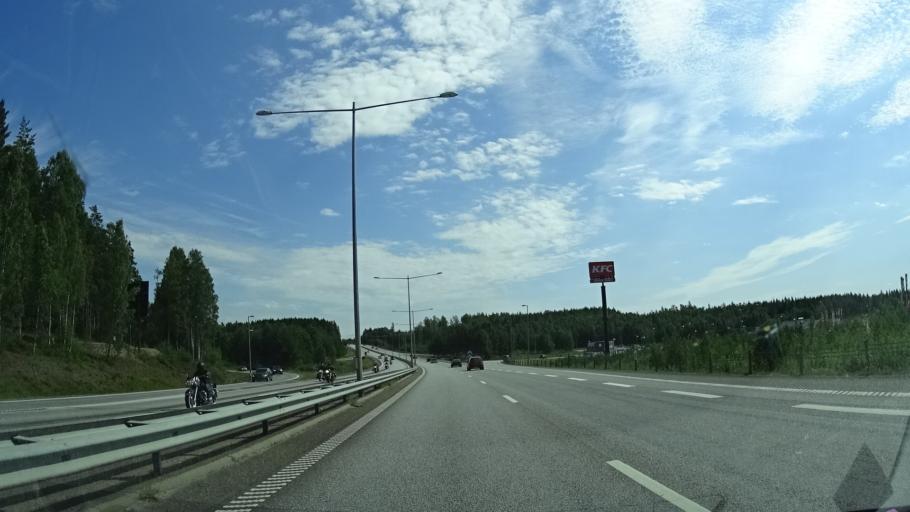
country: SE
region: Vaermland
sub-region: Karlstads Kommun
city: Skattkarr
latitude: 59.3978
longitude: 13.5759
